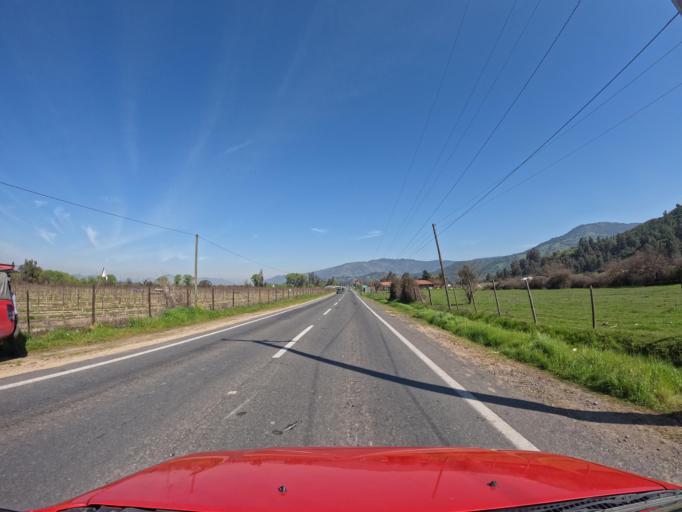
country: CL
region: Maule
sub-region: Provincia de Curico
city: Rauco
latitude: -34.9784
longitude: -71.3951
